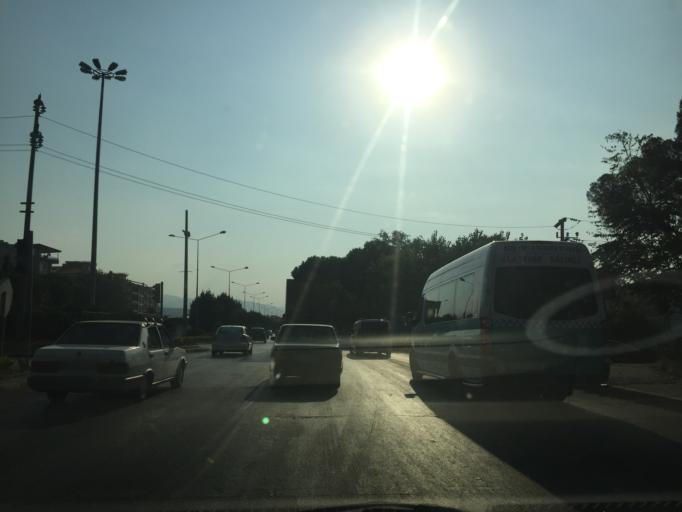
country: TR
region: Manisa
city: Salihli
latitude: 38.4907
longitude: 28.1618
